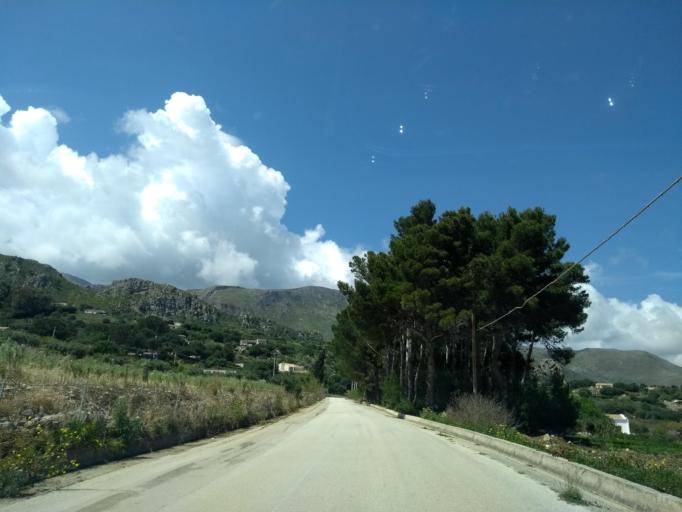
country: IT
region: Sicily
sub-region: Trapani
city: Castellammare del Golfo
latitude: 38.0651
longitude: 12.8218
